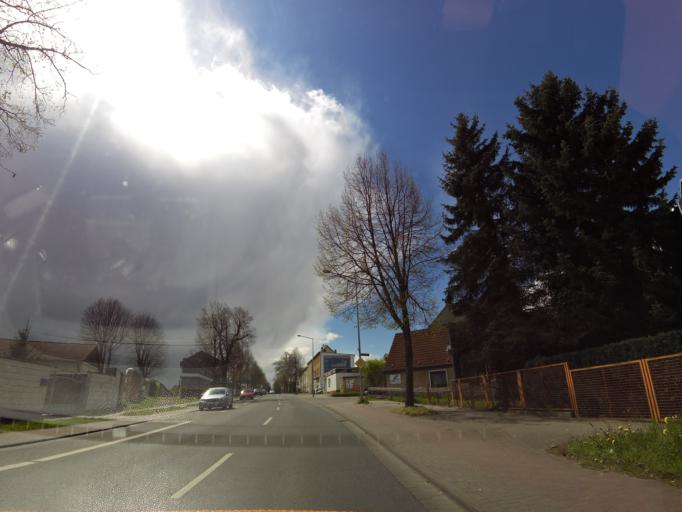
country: DE
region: Saxony-Anhalt
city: Diesdorf
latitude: 52.0978
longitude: 11.5745
